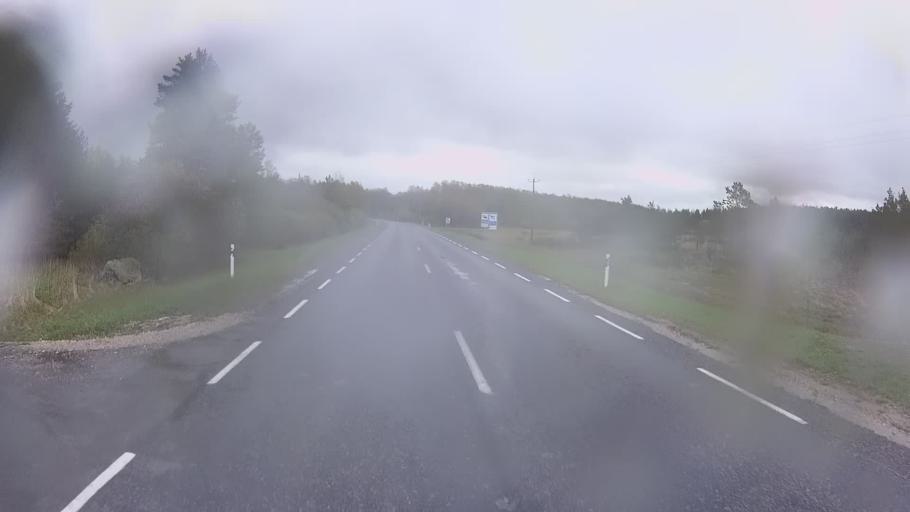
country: EE
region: Hiiumaa
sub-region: Kaerdla linn
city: Kardla
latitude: 58.8330
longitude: 22.8159
